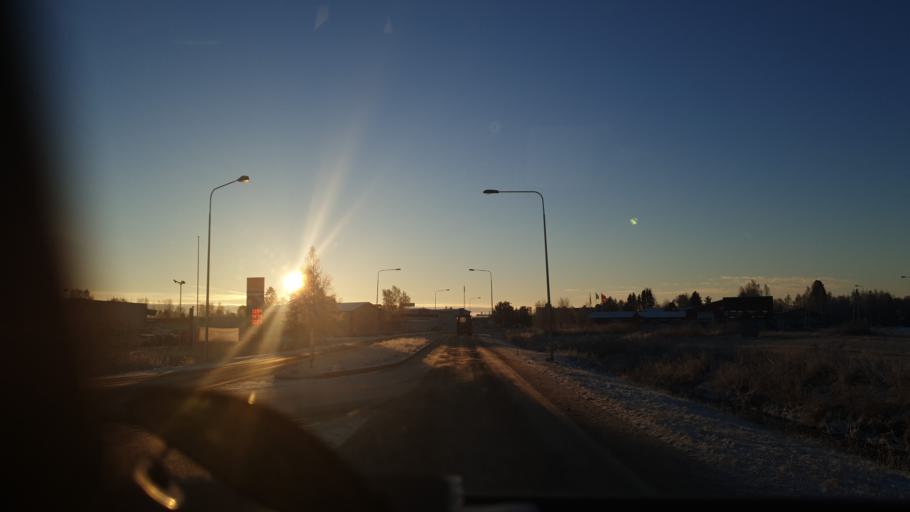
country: FI
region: Northern Ostrobothnia
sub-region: Ylivieska
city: Kalajoki
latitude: 64.2650
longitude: 23.9492
